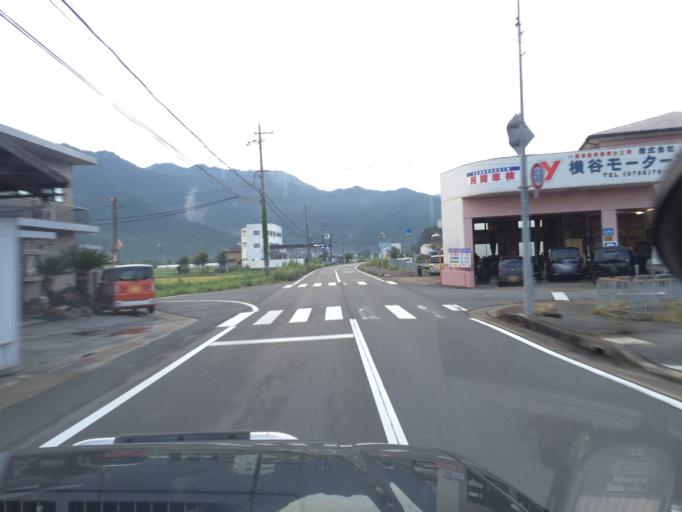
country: JP
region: Hyogo
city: Nishiwaki
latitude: 35.1051
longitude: 134.9945
